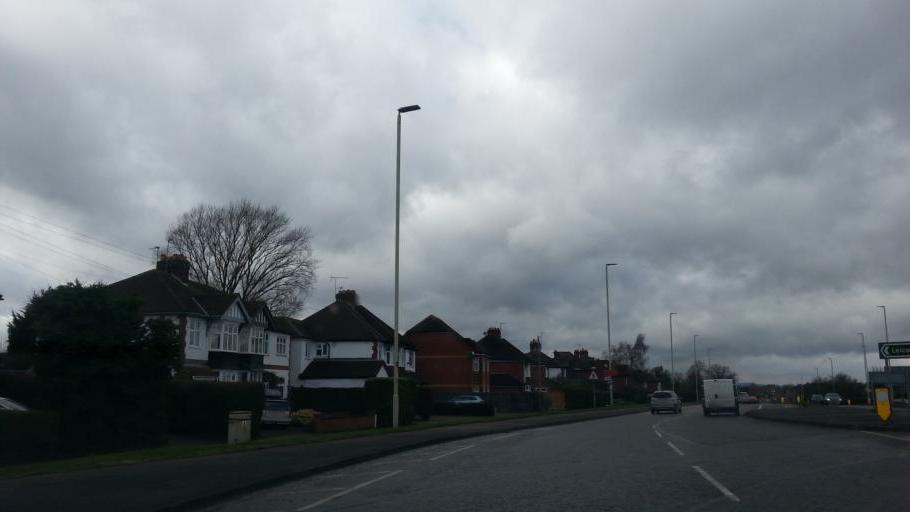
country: GB
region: England
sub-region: Leicestershire
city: Oadby
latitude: 52.5897
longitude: -1.0640
